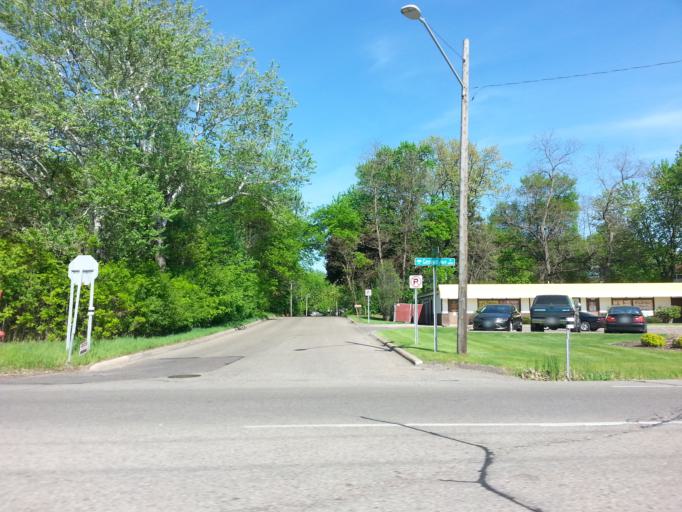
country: US
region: Minnesota
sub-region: Ramsey County
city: North Saint Paul
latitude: 45.0186
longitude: -92.9849
